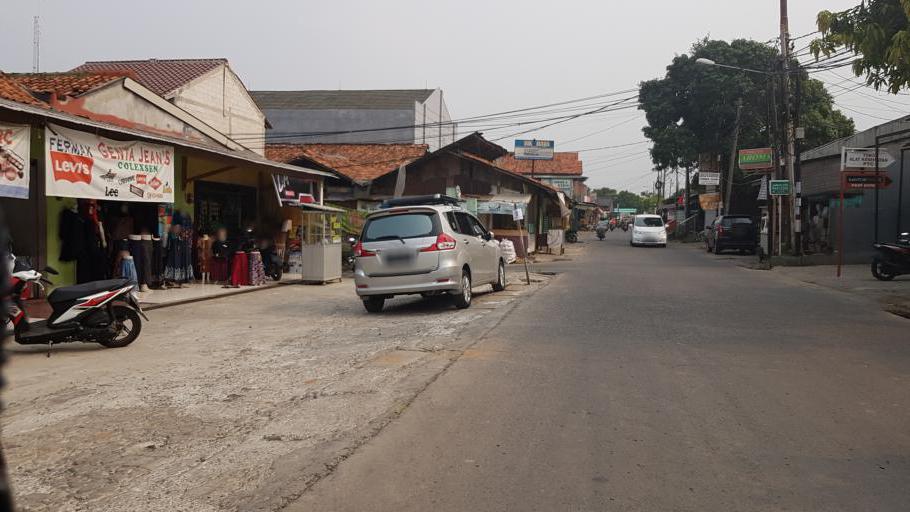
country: ID
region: West Java
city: Depok
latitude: -6.3661
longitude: 106.8431
